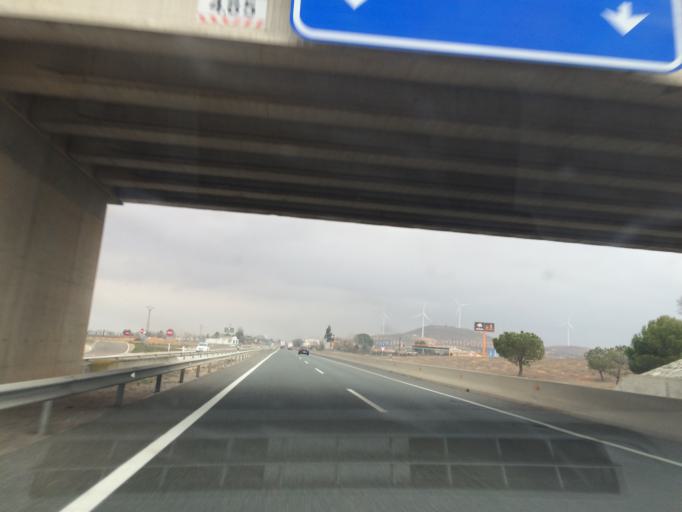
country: ES
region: Castille-La Mancha
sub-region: Province of Toledo
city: Madridejos
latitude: 39.5132
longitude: -3.5247
